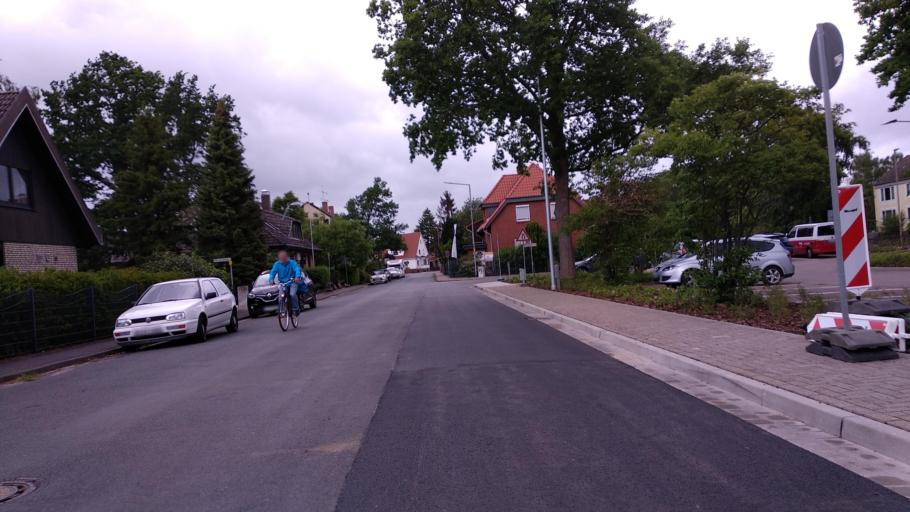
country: DE
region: Lower Saxony
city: Hagenburg
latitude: 52.4581
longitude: 9.3674
